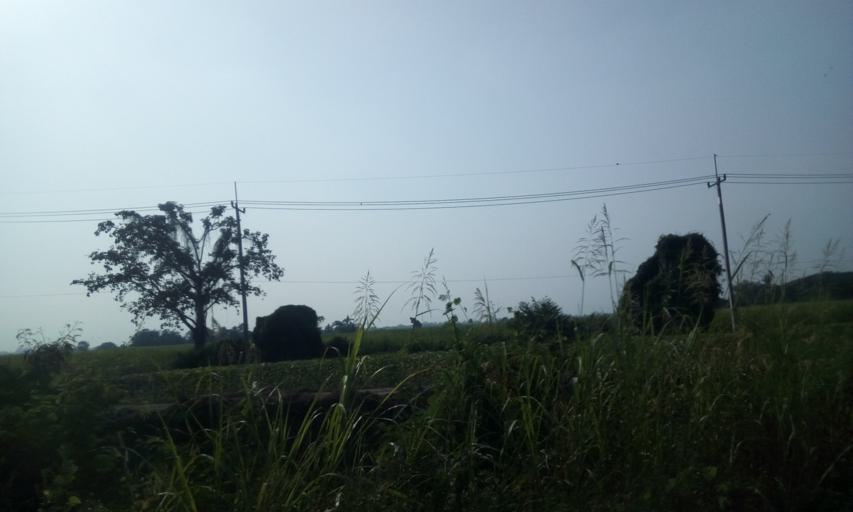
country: TH
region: Sing Buri
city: Phrom Buri
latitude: 14.7479
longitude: 100.4411
